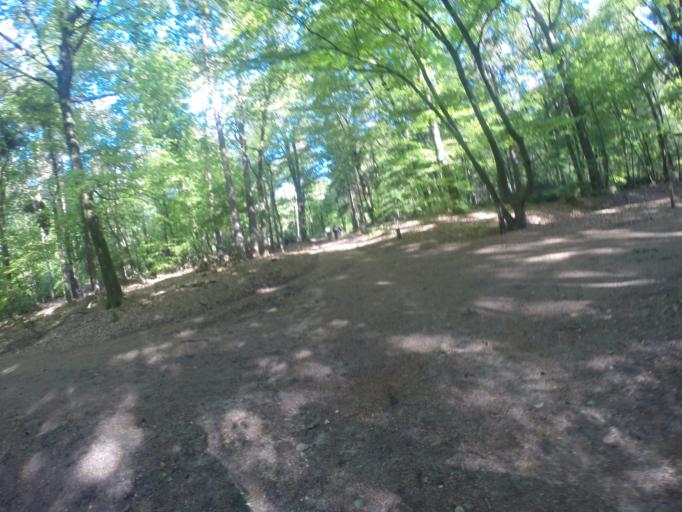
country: NL
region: Gelderland
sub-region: Gemeente Montferland
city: s-Heerenberg
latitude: 51.9056
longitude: 6.2180
